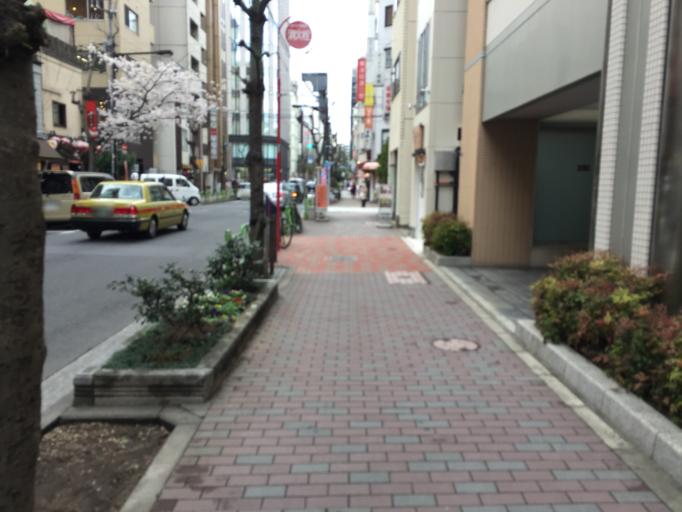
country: JP
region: Tokyo
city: Tokyo
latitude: 35.6711
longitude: 139.7698
